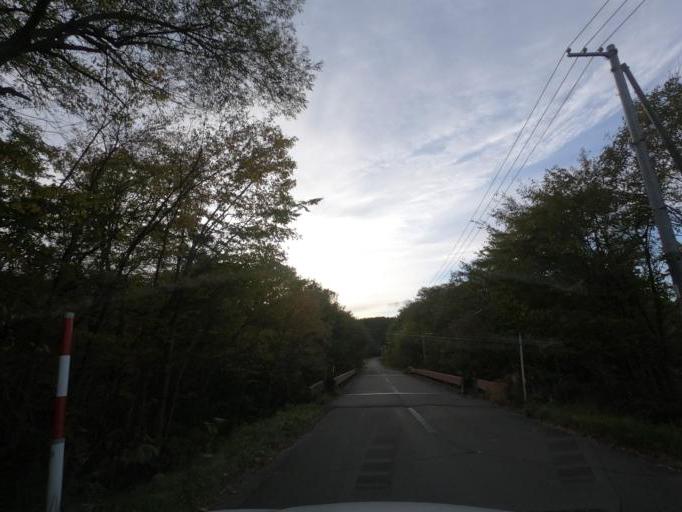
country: JP
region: Hokkaido
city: Obihiro
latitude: 42.5450
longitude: 143.4001
